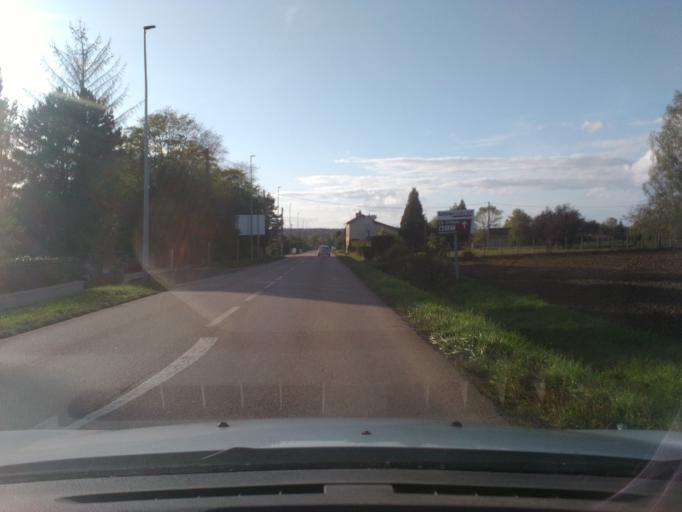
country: FR
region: Lorraine
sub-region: Departement des Vosges
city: Rambervillers
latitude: 48.3417
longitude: 6.6501
